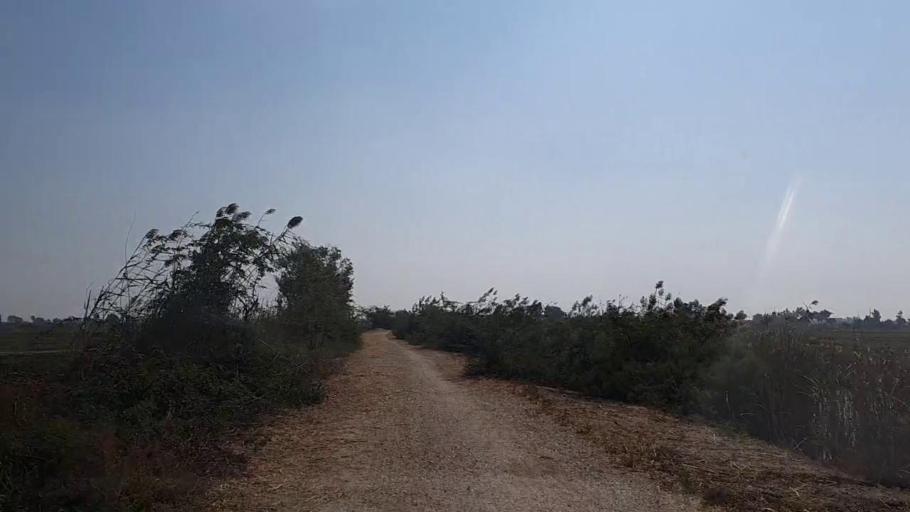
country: PK
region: Sindh
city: Thatta
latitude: 24.7961
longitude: 67.9687
